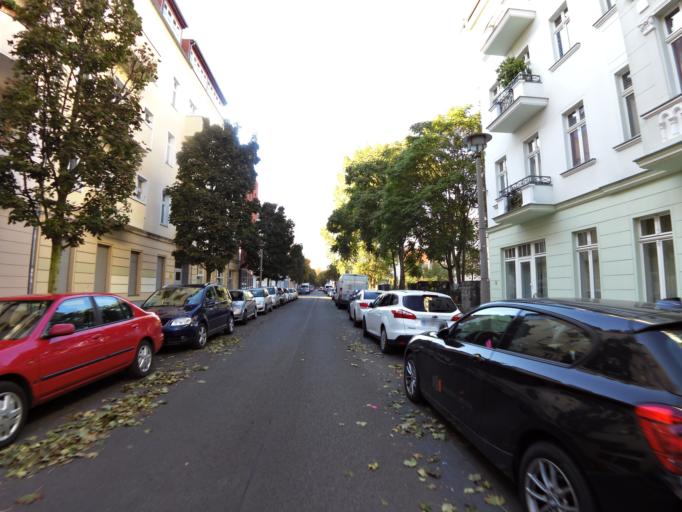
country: DE
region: Berlin
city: Oberschoneweide
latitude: 52.4611
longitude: 13.5247
